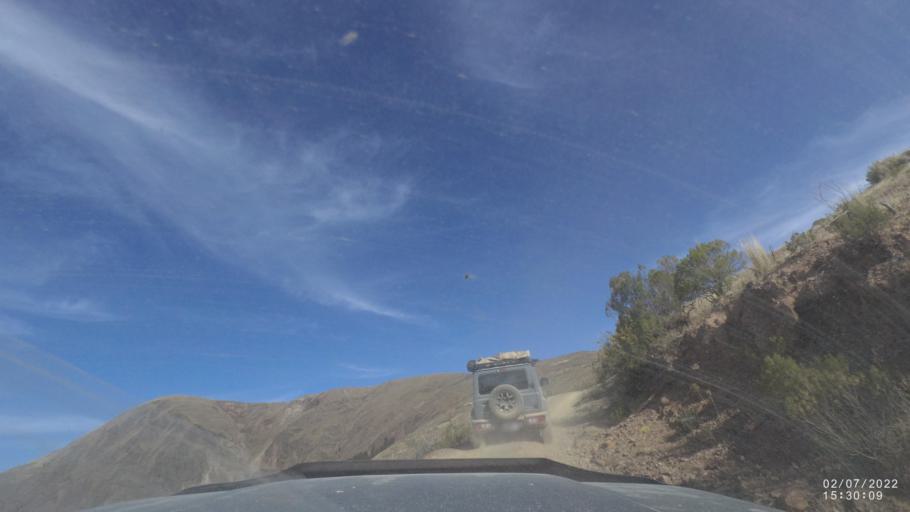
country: BO
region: Cochabamba
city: Irpa Irpa
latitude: -17.8806
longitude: -66.4136
